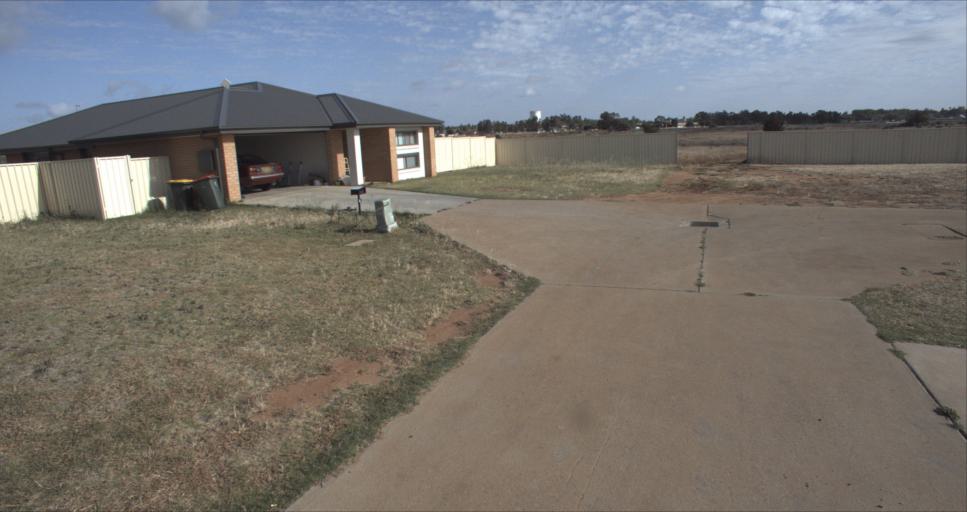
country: AU
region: New South Wales
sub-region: Leeton
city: Leeton
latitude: -34.5696
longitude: 146.4005
